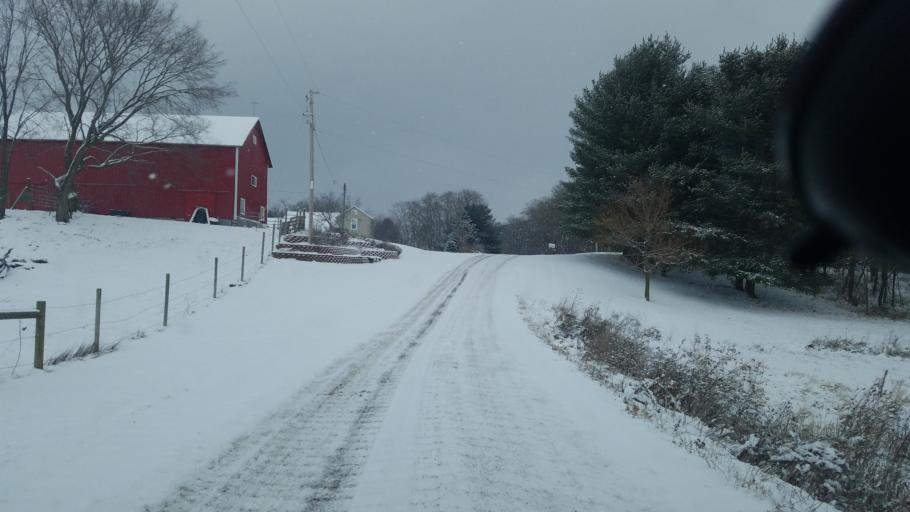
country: US
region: Ohio
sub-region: Richland County
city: Lexington
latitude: 40.7018
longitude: -82.6428
